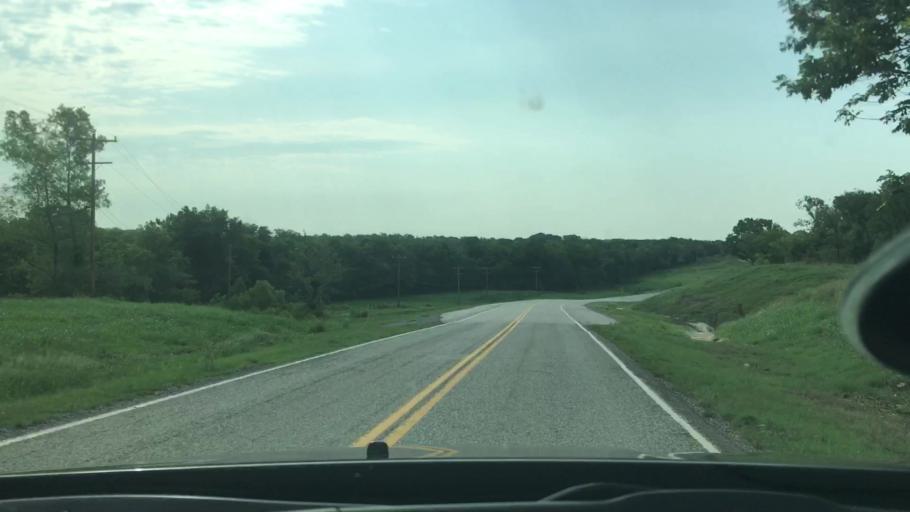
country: US
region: Oklahoma
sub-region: Johnston County
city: Tishomingo
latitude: 34.1633
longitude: -96.5688
